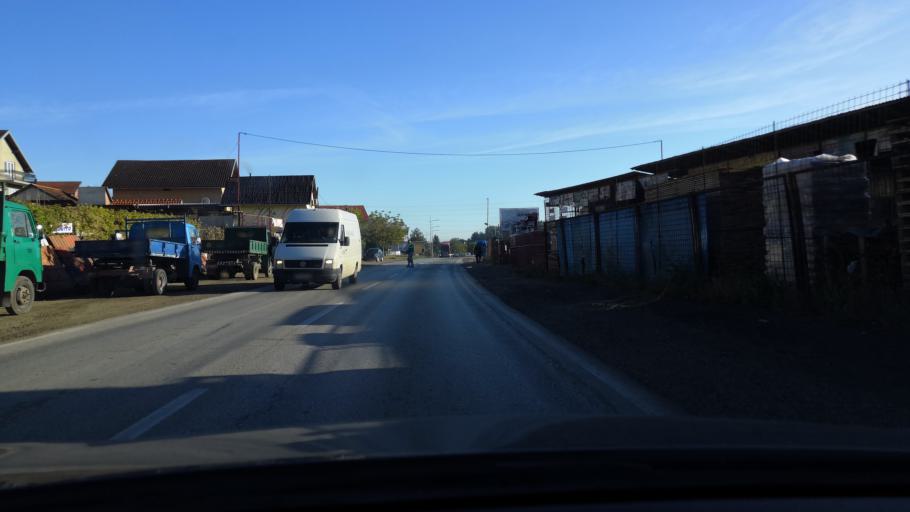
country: RS
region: Autonomna Pokrajina Vojvodina
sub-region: Juznobacki Okrug
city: Petrovaradin
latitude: 45.2284
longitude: 19.8810
